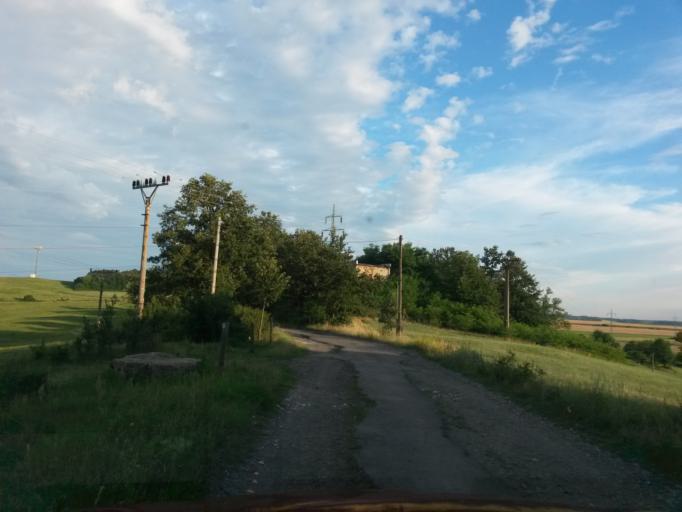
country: SK
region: Banskobystricky
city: Lucenec
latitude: 48.2894
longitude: 19.5020
